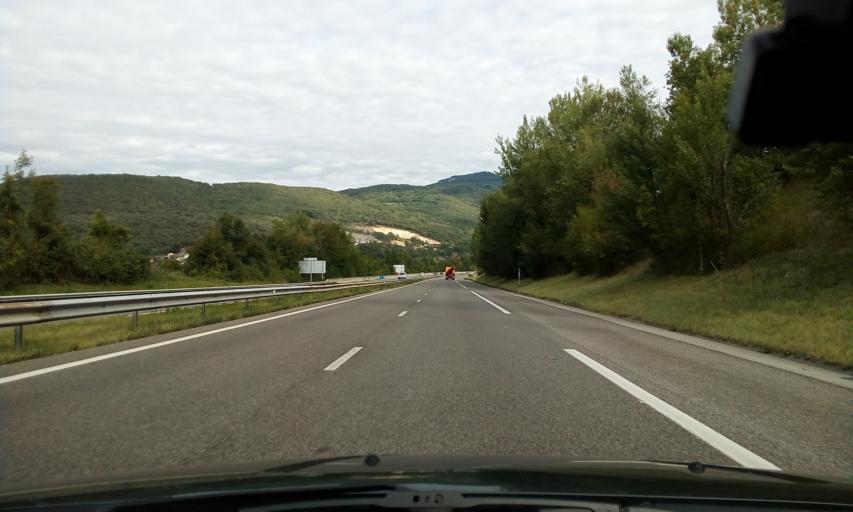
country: FR
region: Rhone-Alpes
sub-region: Departement de la Savoie
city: Gresy-sur-Aix
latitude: 45.7065
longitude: 5.9269
